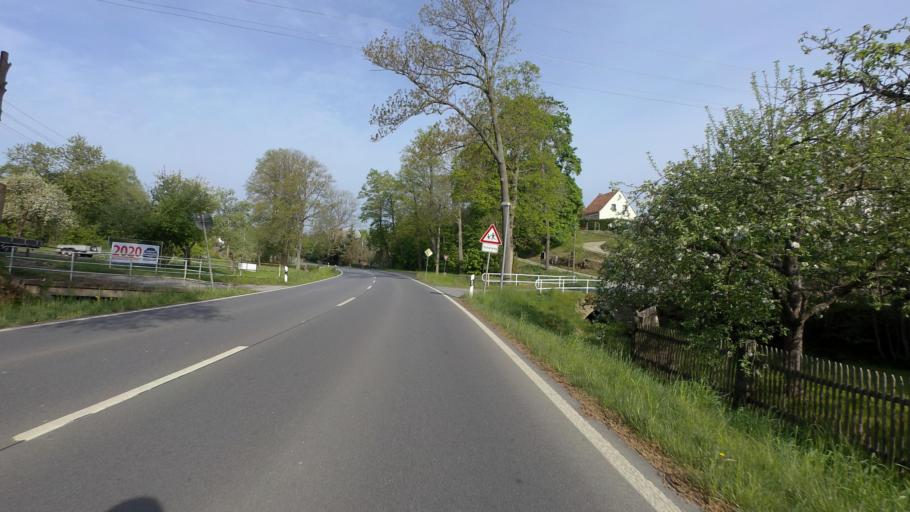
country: DE
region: Saxony
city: Stolpen
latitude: 51.0424
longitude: 14.1147
